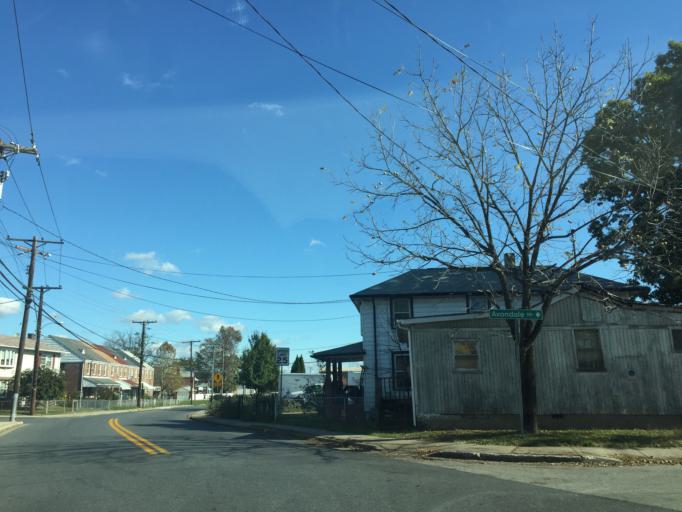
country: US
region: Maryland
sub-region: Baltimore County
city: Dundalk
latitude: 39.2436
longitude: -76.5104
